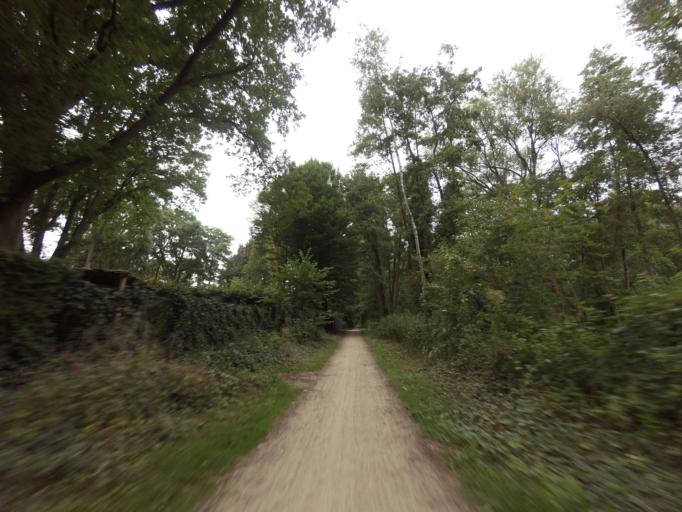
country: BE
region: Flanders
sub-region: Provincie Antwerpen
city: Schilde
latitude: 51.2456
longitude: 4.5999
